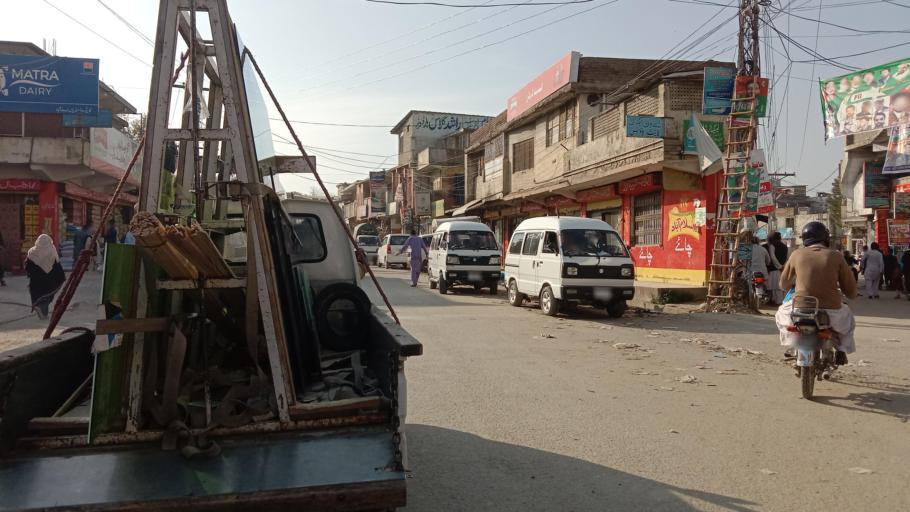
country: PK
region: Khyber Pakhtunkhwa
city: Abbottabad
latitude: 34.1974
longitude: 73.2323
